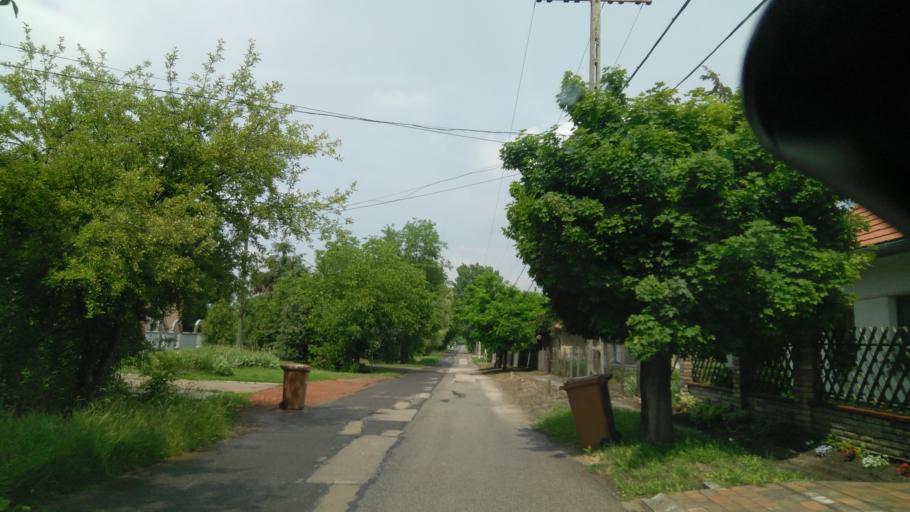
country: HU
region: Bekes
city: Bekescsaba
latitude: 46.6665
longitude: 21.1731
